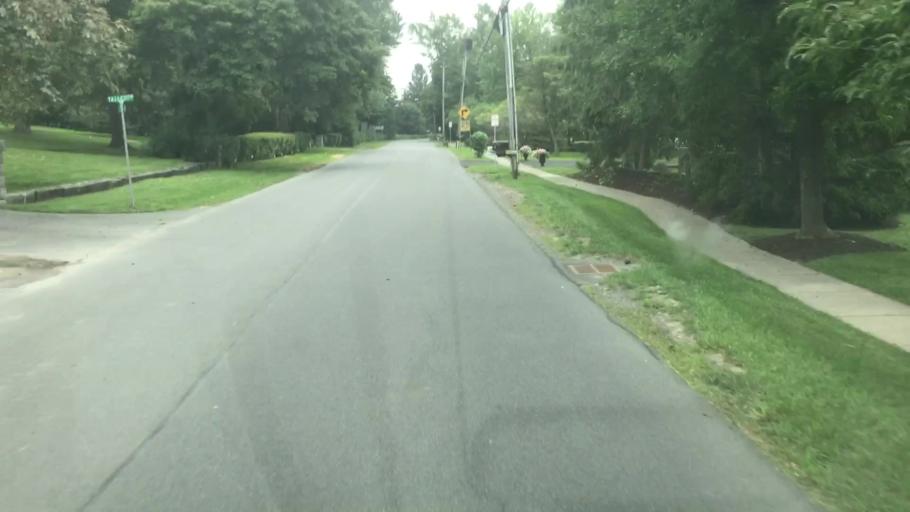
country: US
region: New York
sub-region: Onondaga County
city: Skaneateles
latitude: 42.9378
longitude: -76.4321
